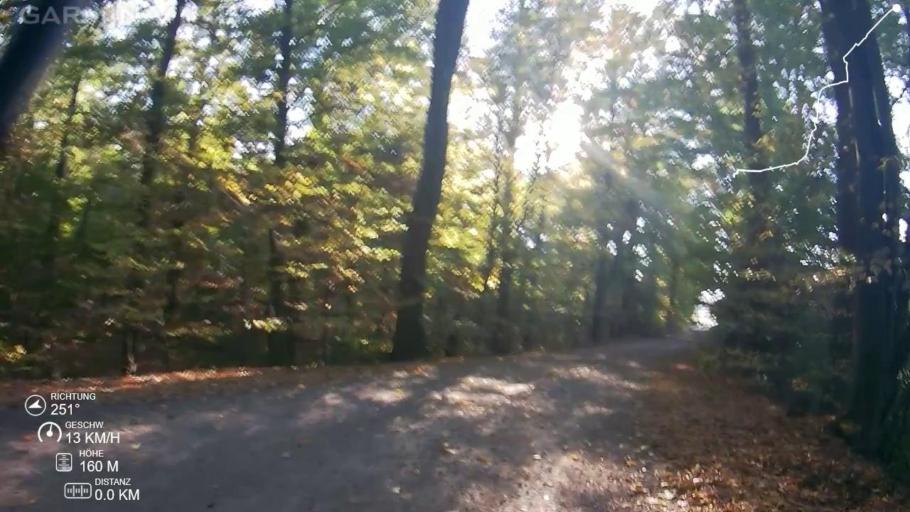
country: DE
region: Hesse
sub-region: Regierungsbezirk Darmstadt
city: Darmstadt
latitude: 49.9131
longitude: 8.6891
